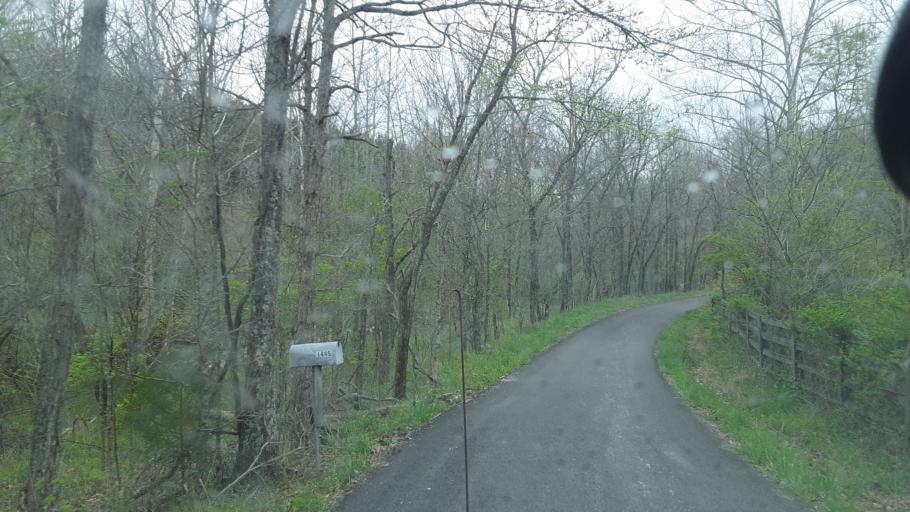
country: US
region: Kentucky
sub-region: Owen County
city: Owenton
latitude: 38.6618
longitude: -84.7878
